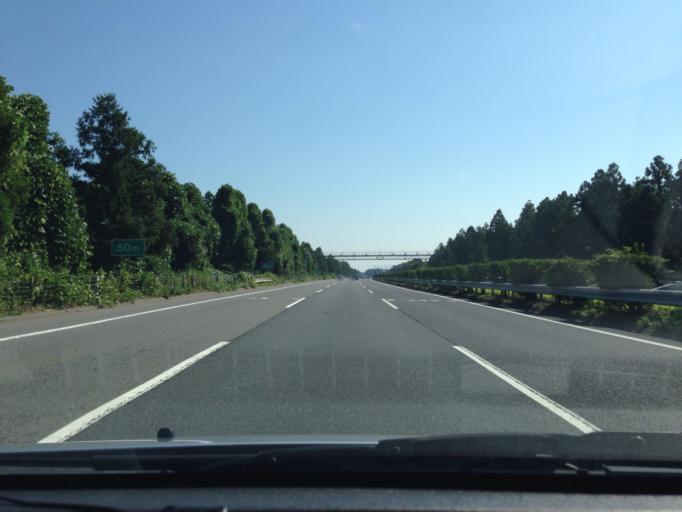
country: JP
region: Ibaraki
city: Ishioka
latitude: 36.1327
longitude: 140.1964
